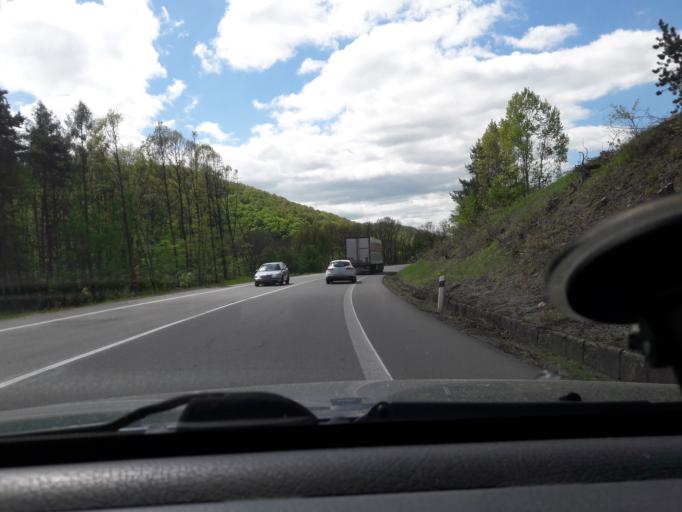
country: SK
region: Banskobystricky
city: Krupina
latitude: 48.3884
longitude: 19.0848
